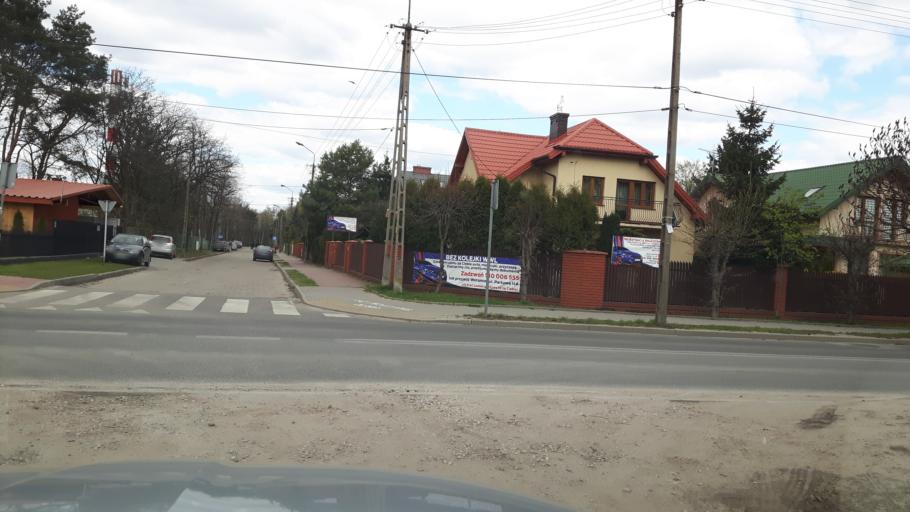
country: PL
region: Masovian Voivodeship
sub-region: Powiat wolominski
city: Wolomin
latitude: 52.3464
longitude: 21.2241
